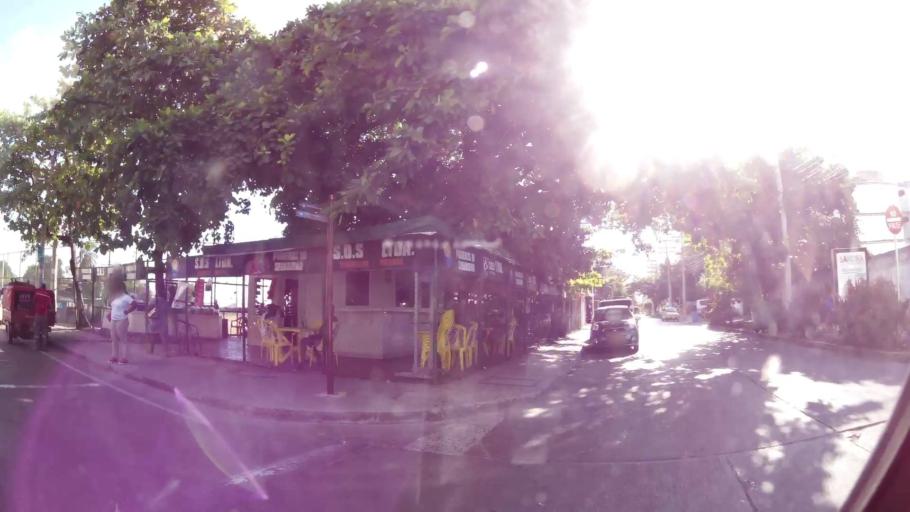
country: CO
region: Bolivar
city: Cartagena
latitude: 10.3967
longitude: -75.5569
